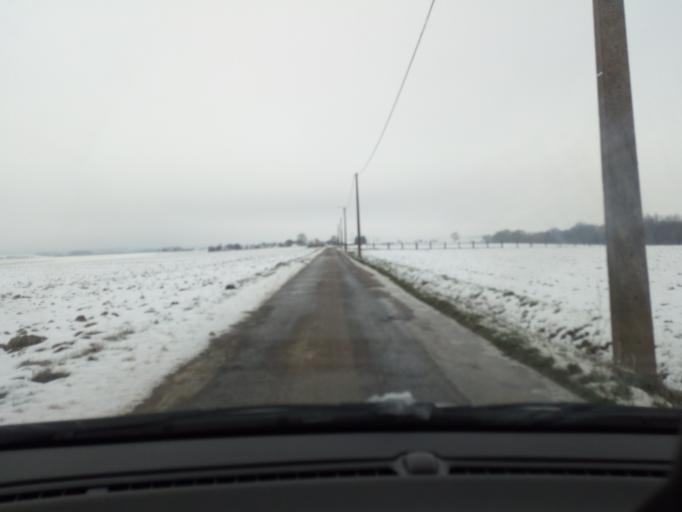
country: FR
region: Nord-Pas-de-Calais
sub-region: Departement du Nord
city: Boussois
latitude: 50.3599
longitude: 4.0259
